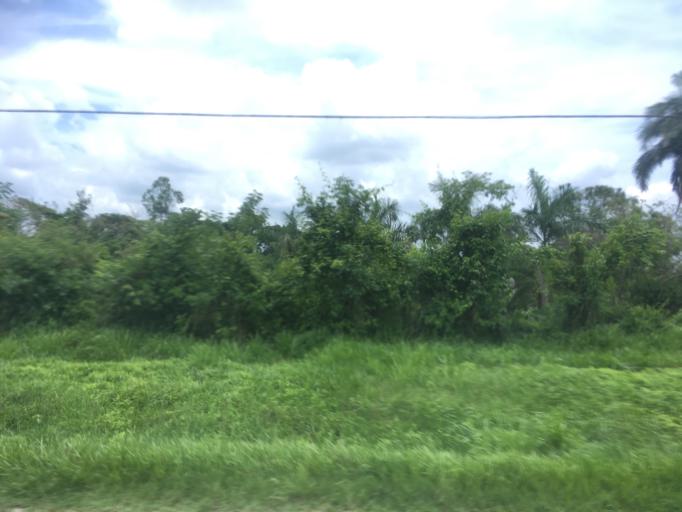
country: CU
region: Villa Clara
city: Esperanza
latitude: 22.4221
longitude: -80.0489
